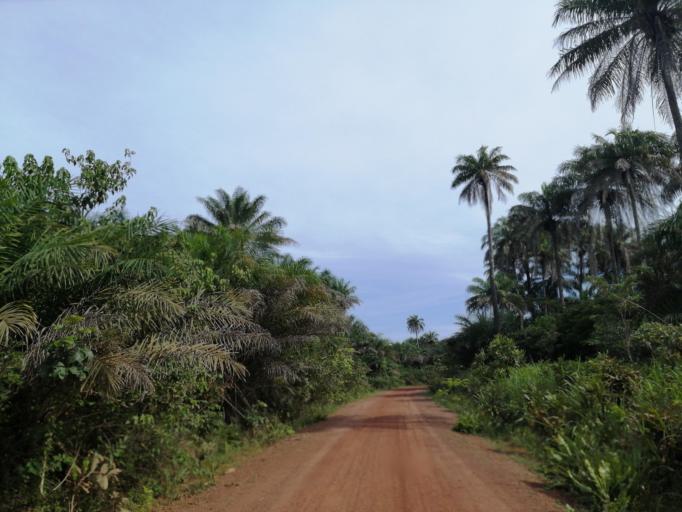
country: SL
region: Northern Province
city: Port Loko
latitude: 8.7776
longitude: -12.9194
